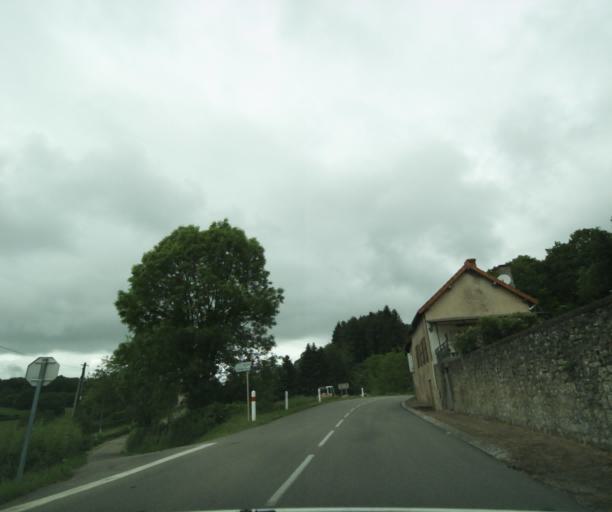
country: FR
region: Bourgogne
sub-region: Departement de Saone-et-Loire
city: Charolles
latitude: 46.4455
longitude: 4.2711
